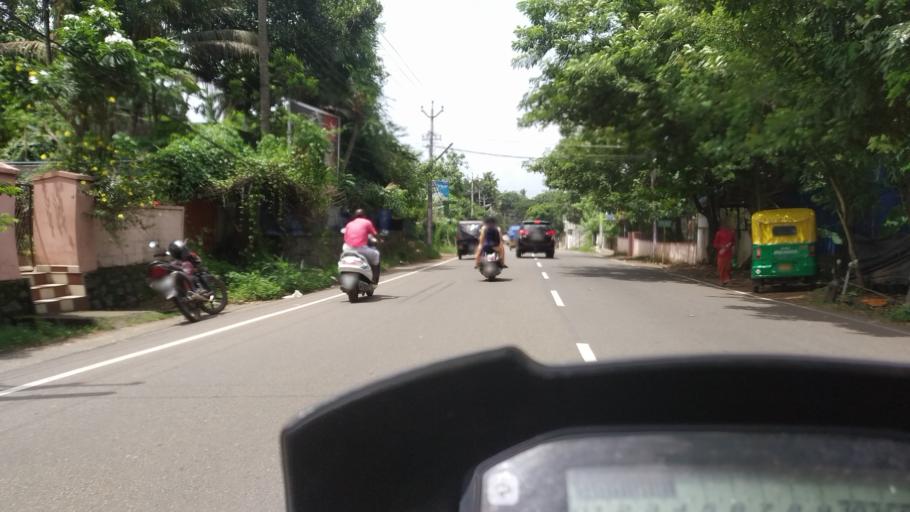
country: IN
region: Kerala
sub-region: Ernakulam
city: Aluva
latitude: 10.1265
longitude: 76.3263
